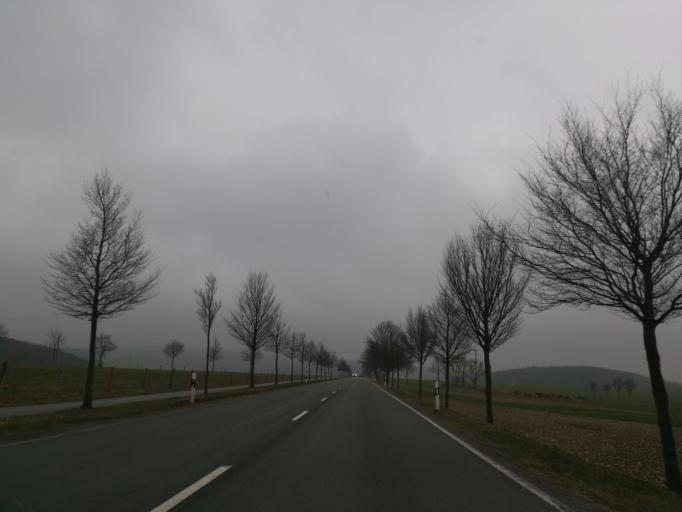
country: DE
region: North Rhine-Westphalia
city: Lichtenau
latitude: 51.5953
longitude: 8.8856
